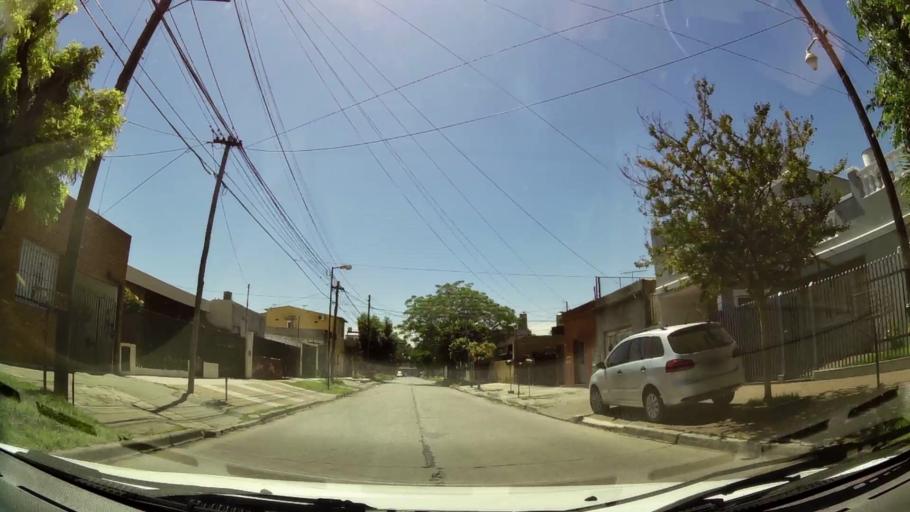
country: AR
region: Buenos Aires
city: Caseros
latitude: -34.5684
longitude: -58.5696
